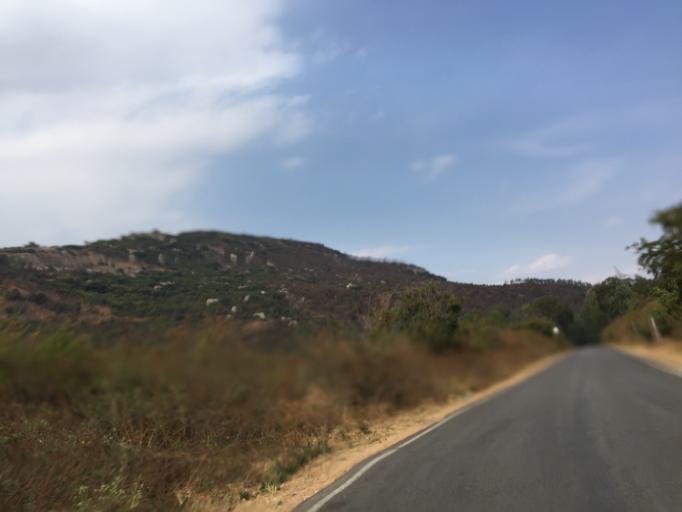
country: IN
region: Karnataka
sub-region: Chikkaballapur
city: Chik Ballapur
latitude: 13.3702
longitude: 77.6627
